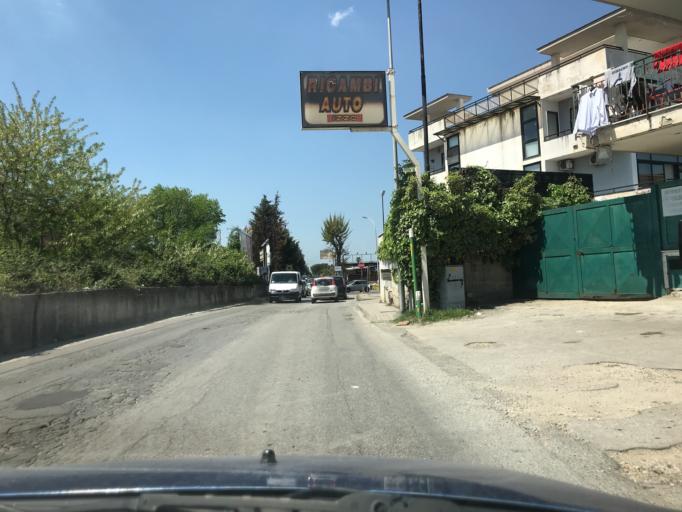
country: IT
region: Campania
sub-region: Provincia di Napoli
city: Calvizzano
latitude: 40.9089
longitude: 14.1964
